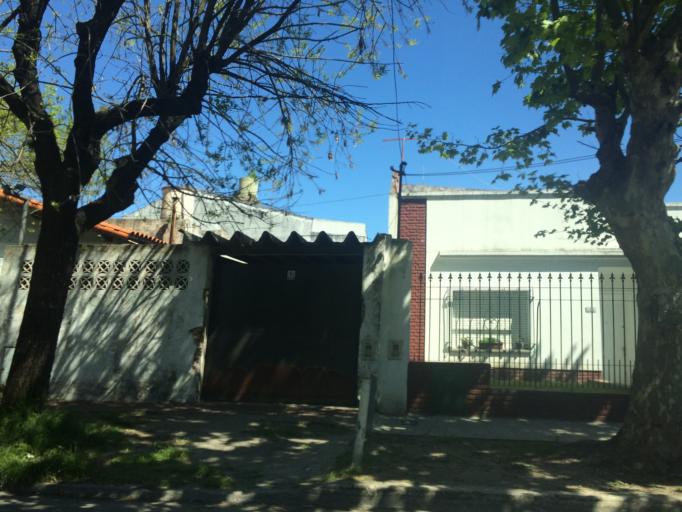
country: AR
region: Buenos Aires
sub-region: Partido de Lanus
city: Lanus
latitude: -34.7198
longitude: -58.3987
